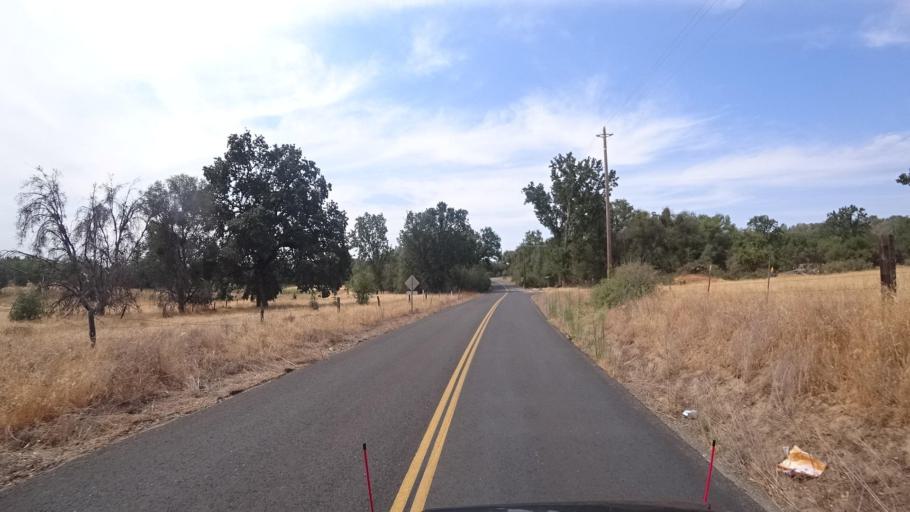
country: US
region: California
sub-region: Mariposa County
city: Mariposa
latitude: 37.4746
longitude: -119.8998
